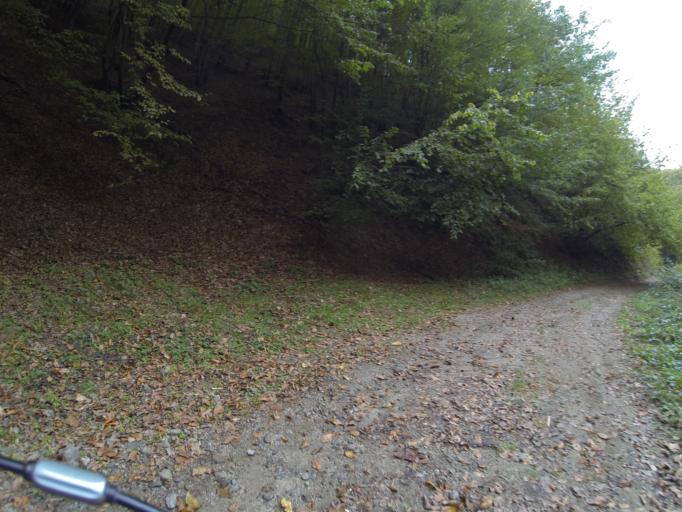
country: RO
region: Gorj
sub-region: Comuna Tismana
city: Sohodol
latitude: 45.0811
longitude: 22.8868
